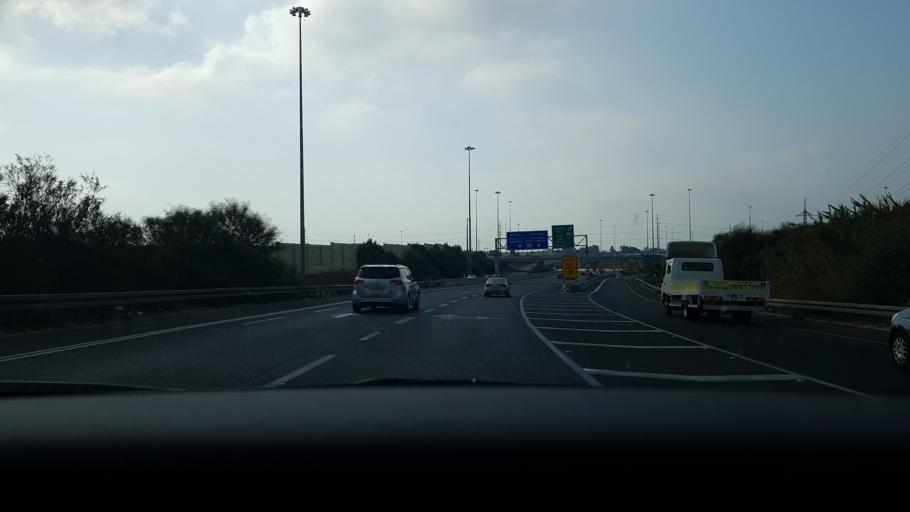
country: IL
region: Central District
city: Rishon LeZiyyon
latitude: 31.9605
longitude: 34.7853
